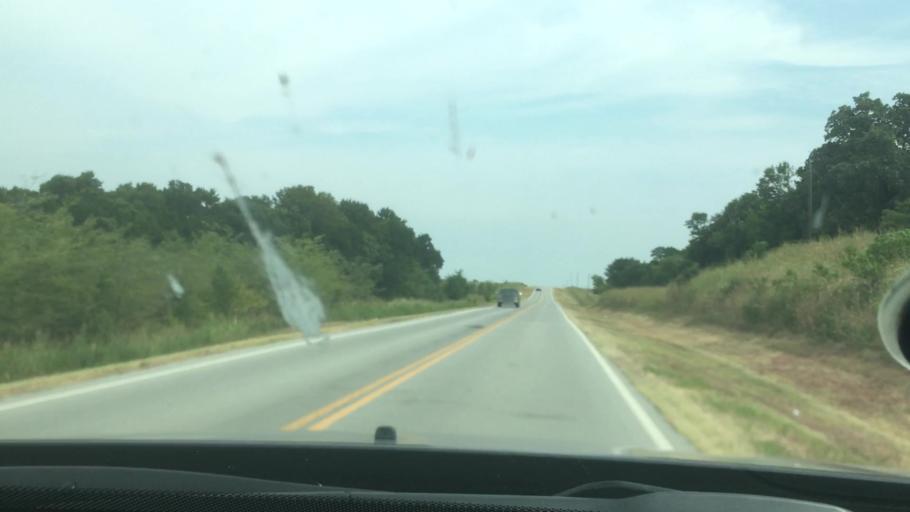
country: US
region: Oklahoma
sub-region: Coal County
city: Coalgate
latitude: 34.5574
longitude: -96.4069
